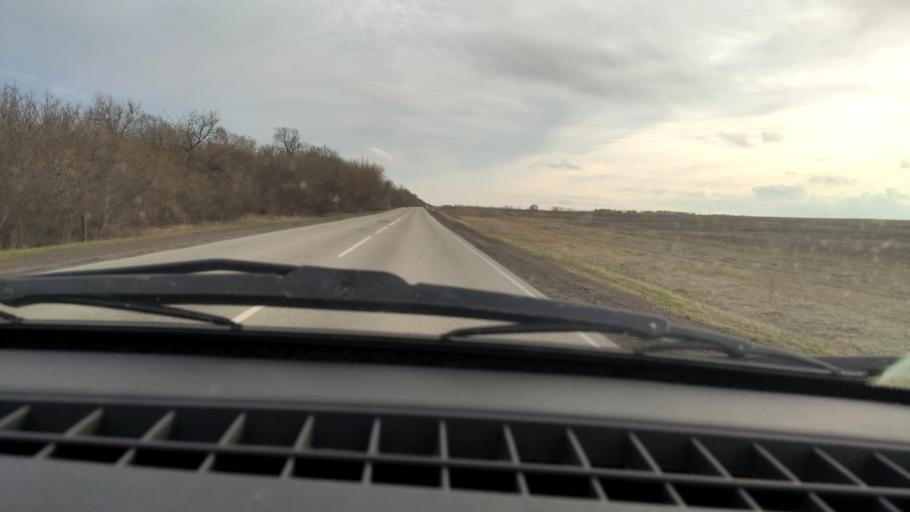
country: RU
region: Bashkortostan
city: Chishmy
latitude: 54.4787
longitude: 55.2675
